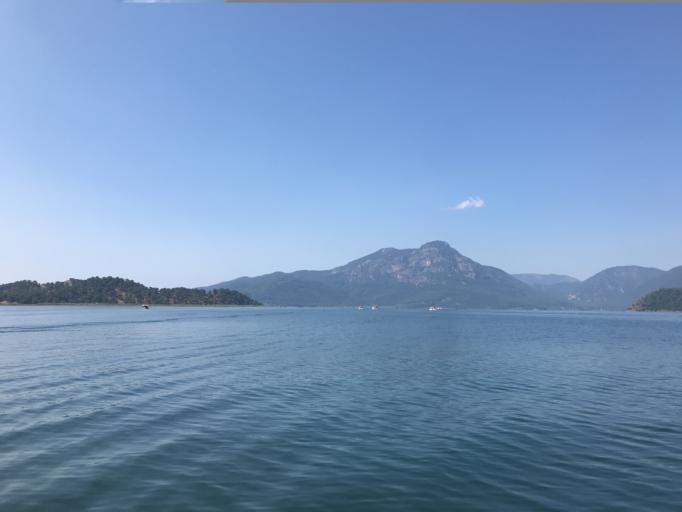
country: TR
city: Dalyan
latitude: 36.9100
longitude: 28.6525
